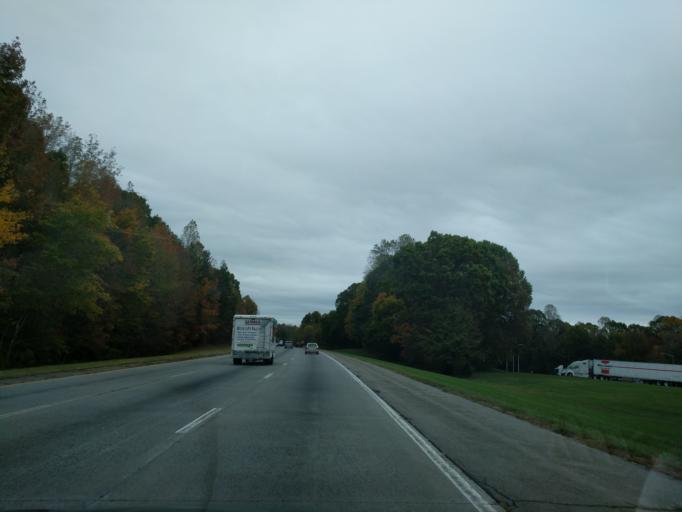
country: US
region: North Carolina
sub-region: Davidson County
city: Thomasville
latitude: 35.8399
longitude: -80.1367
